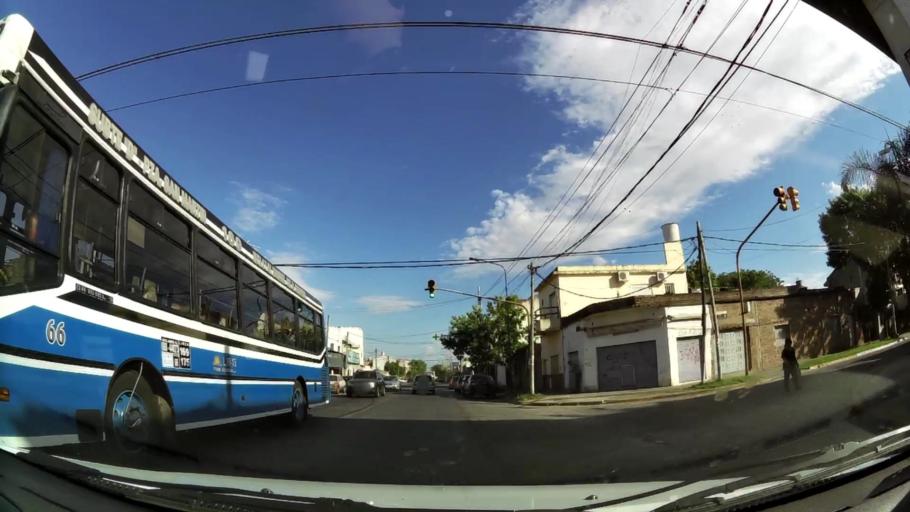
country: AR
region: Buenos Aires
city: Hurlingham
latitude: -34.5726
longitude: -58.6181
